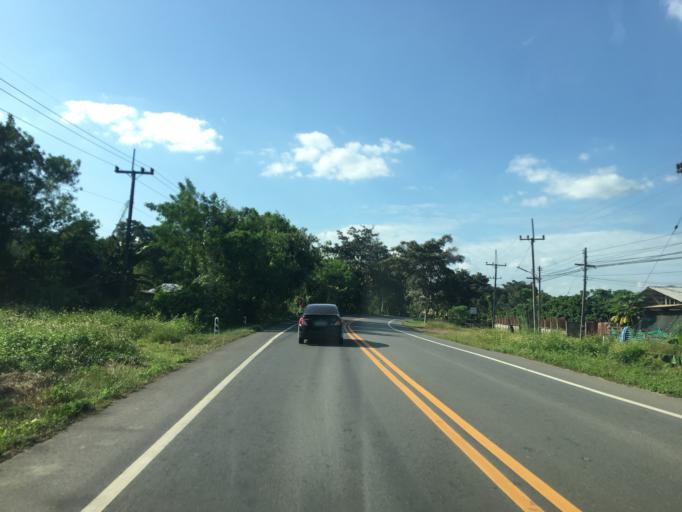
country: TH
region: Phayao
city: Chun
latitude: 19.3546
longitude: 100.0996
